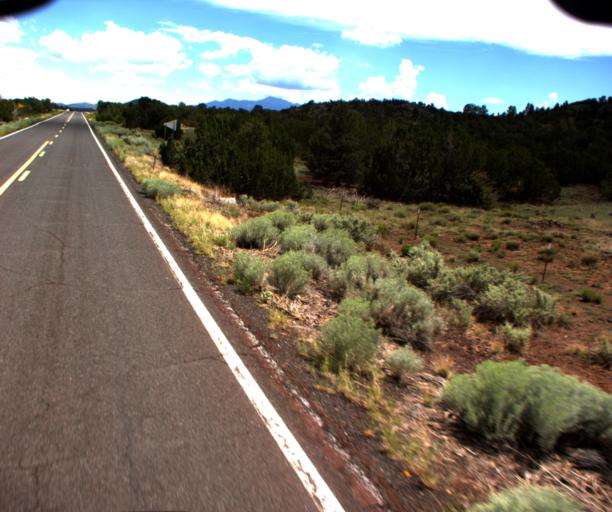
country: US
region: Arizona
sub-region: Coconino County
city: Parks
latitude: 35.5562
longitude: -111.8727
